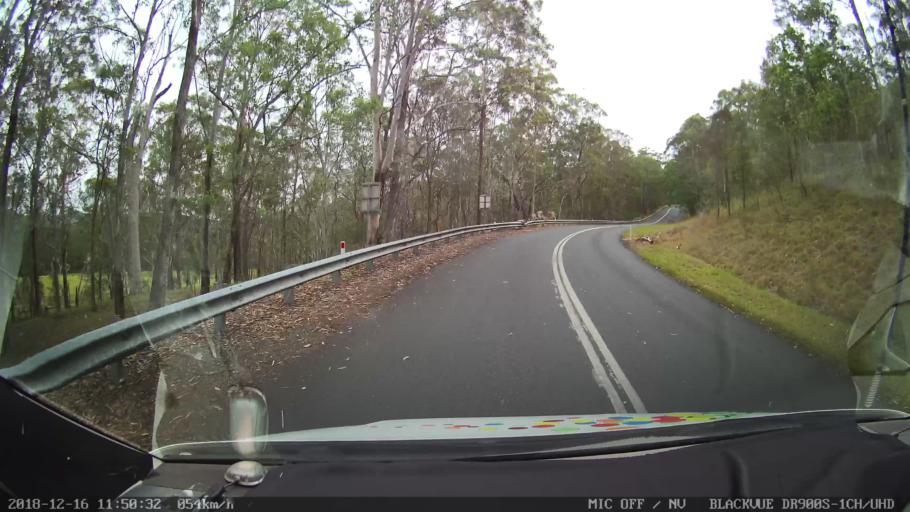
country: AU
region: New South Wales
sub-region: Tenterfield Municipality
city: Carrolls Creek
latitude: -28.9073
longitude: 152.2607
